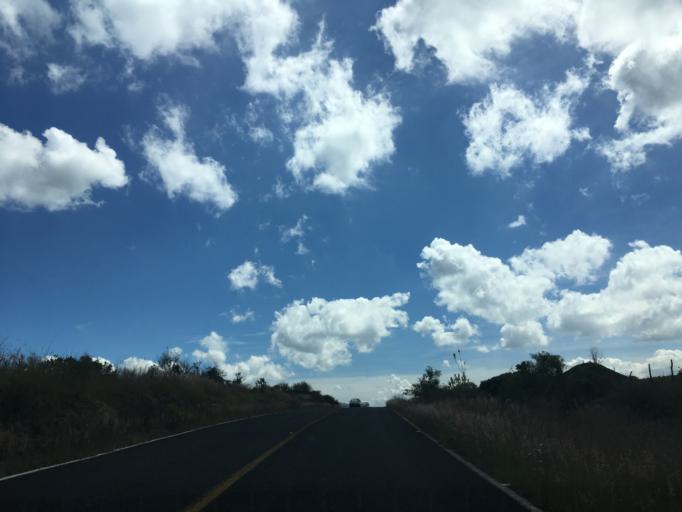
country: MX
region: Michoacan
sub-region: Morelia
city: Cuto de la Esperanza
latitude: 19.7716
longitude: -101.3781
